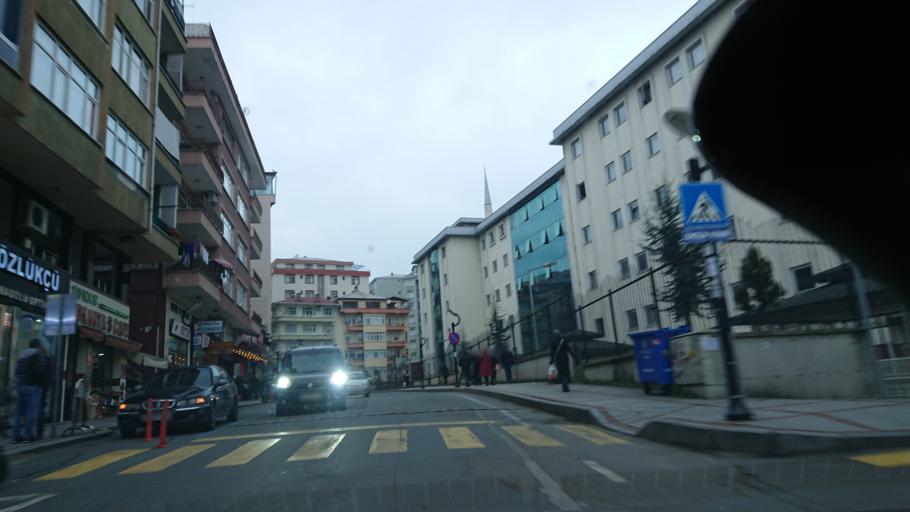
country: TR
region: Rize
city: Rize
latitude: 41.0278
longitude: 40.5142
